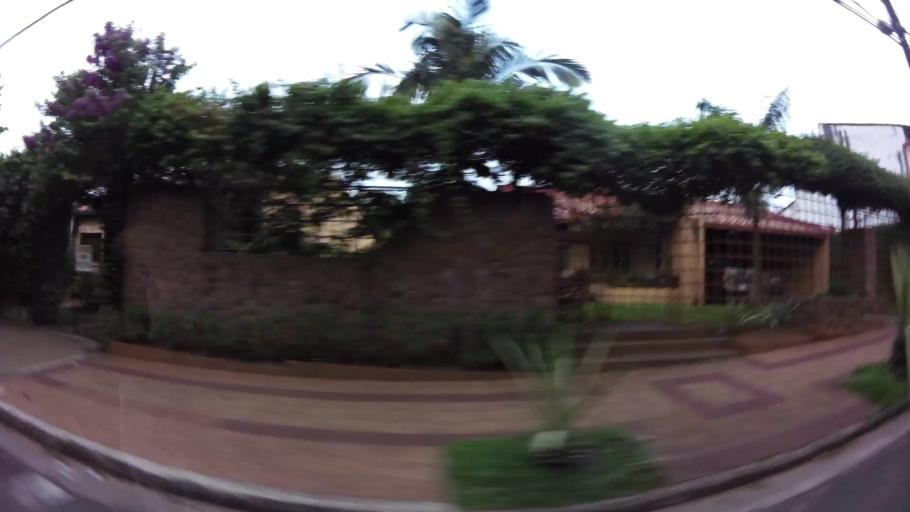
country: PY
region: Central
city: Lambare
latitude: -25.3426
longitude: -57.6159
